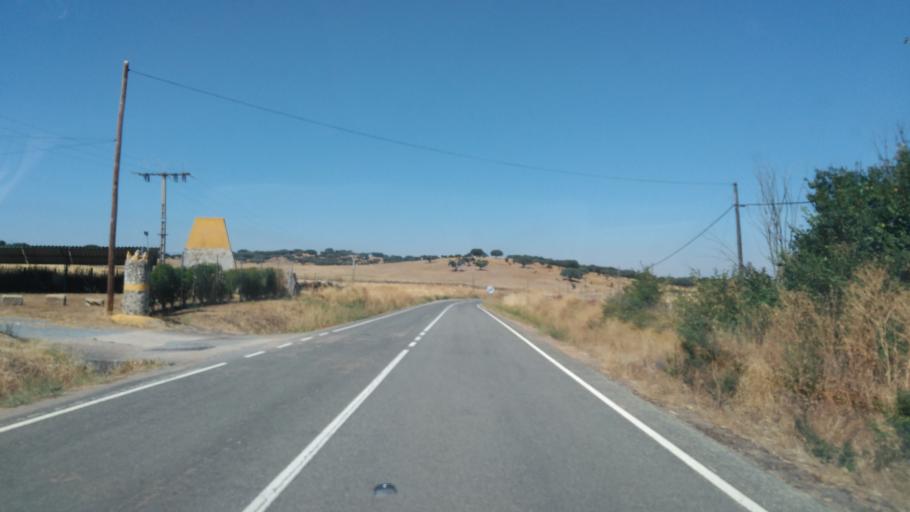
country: ES
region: Castille and Leon
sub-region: Provincia de Salamanca
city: Matilla de los Canos del Rio
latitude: 40.7966
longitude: -5.9183
